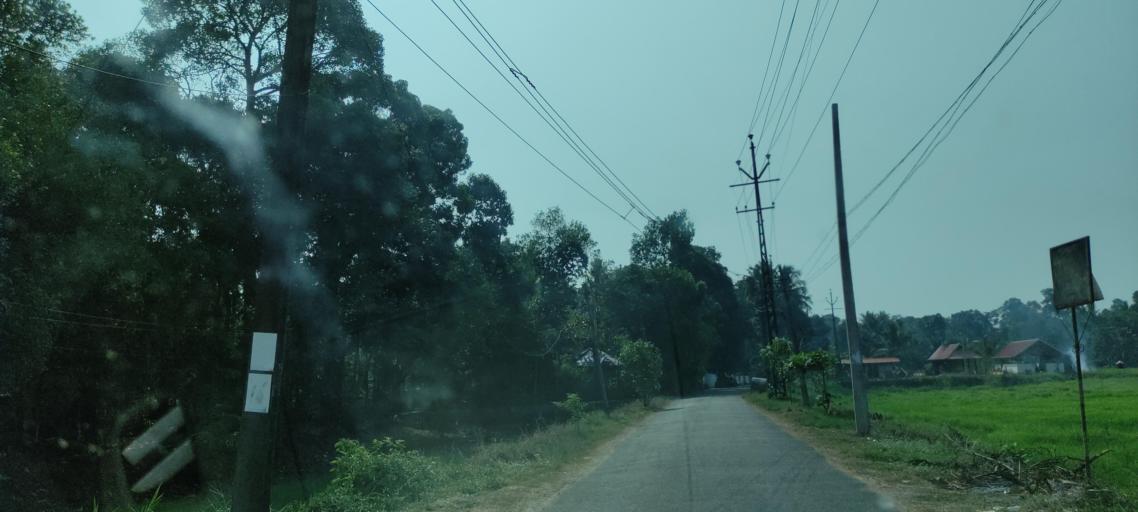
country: IN
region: Kerala
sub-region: Pattanamtitta
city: Tiruvalla
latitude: 9.3596
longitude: 76.5127
